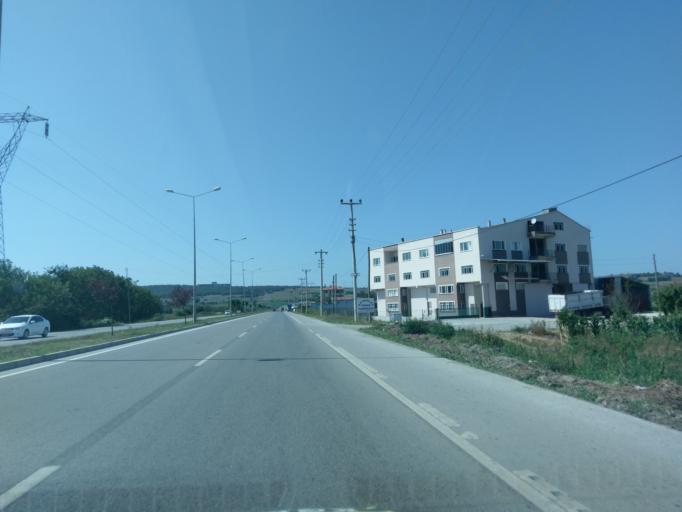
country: TR
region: Samsun
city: Bafra
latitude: 41.5758
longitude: 35.8592
